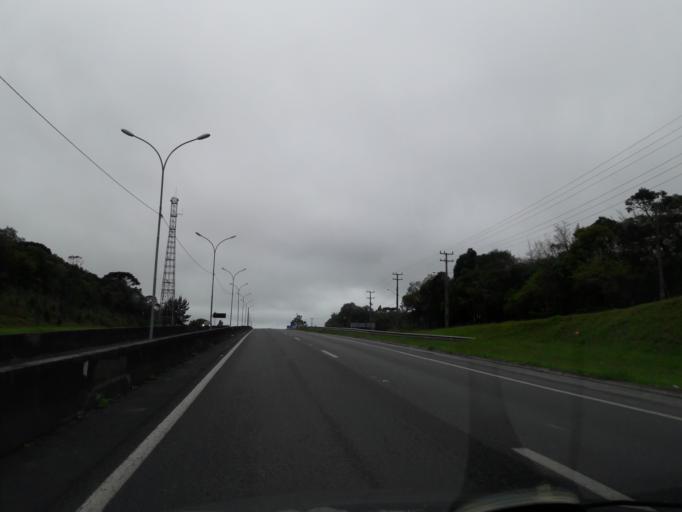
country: BR
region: Parana
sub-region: Quatro Barras
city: Quatro Barras
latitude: -25.3611
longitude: -49.0783
